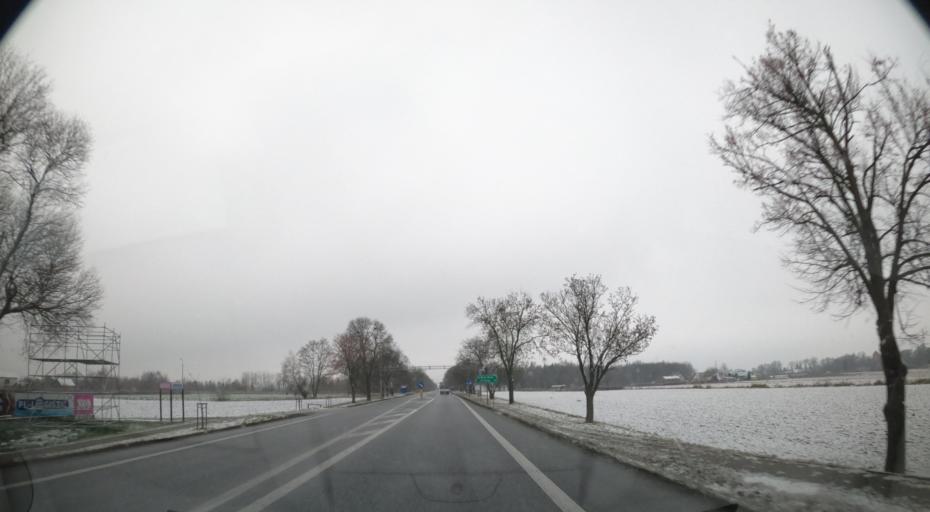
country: PL
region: Masovian Voivodeship
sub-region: Powiat warszawski zachodni
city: Bieniewice
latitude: 52.2027
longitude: 20.5312
